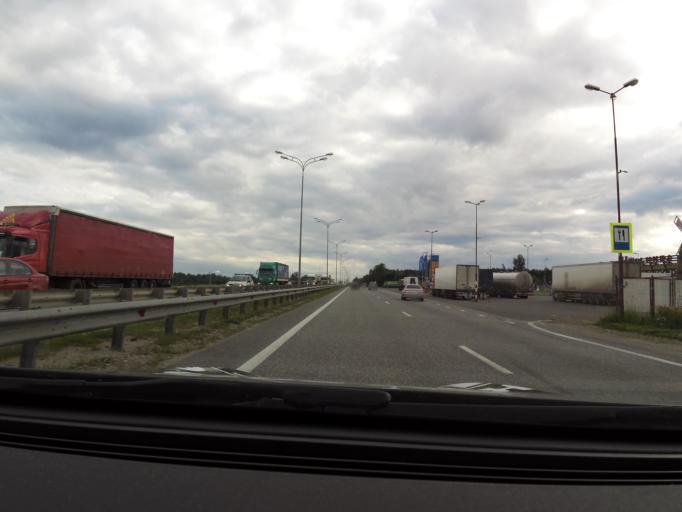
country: RU
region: Tatarstan
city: Osinovo
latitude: 55.7564
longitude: 48.8090
